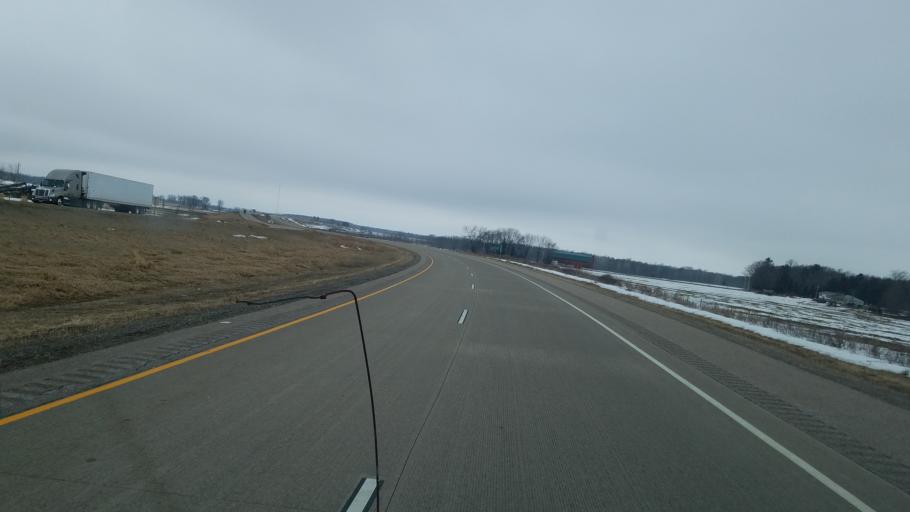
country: US
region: Wisconsin
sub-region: Marathon County
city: Stratford
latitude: 44.6189
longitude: -89.9232
